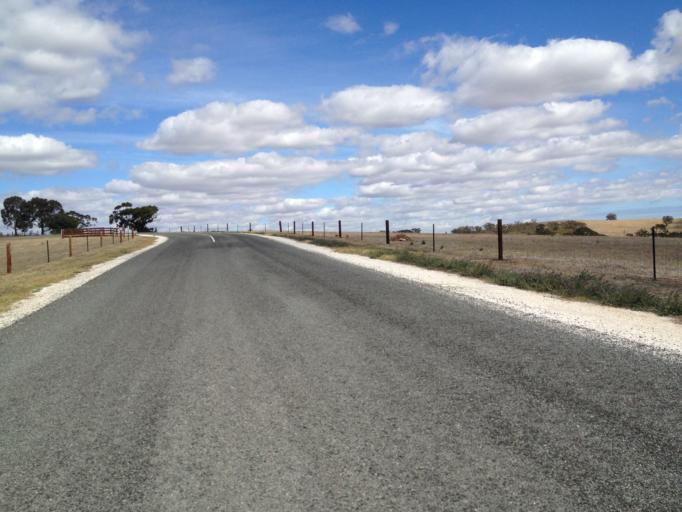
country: AU
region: South Australia
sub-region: Barossa
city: Lyndoch
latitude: -34.6288
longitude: 138.8312
